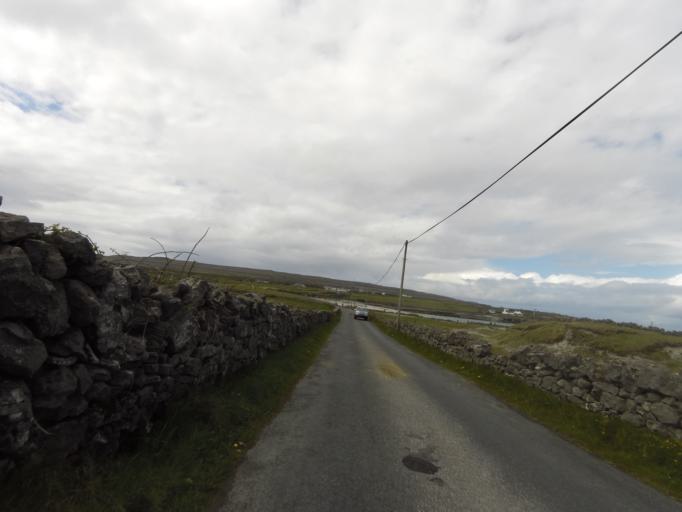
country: IE
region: Connaught
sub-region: County Galway
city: Clifden
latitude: 53.1309
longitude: -9.7452
